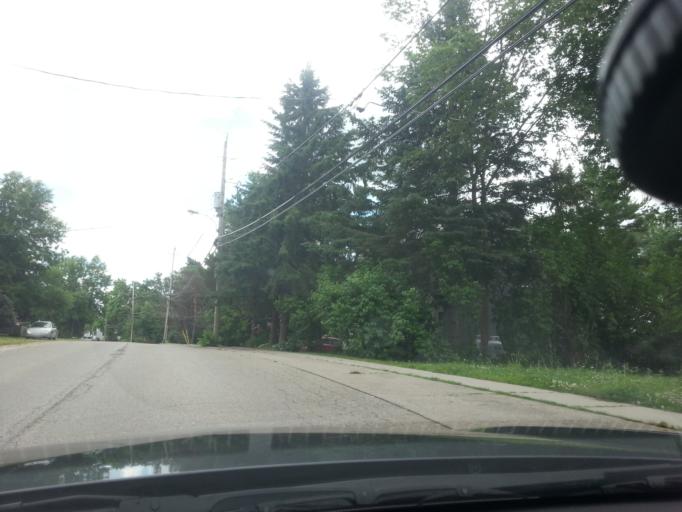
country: CA
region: Ontario
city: Gananoque
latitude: 44.6090
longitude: -76.2254
